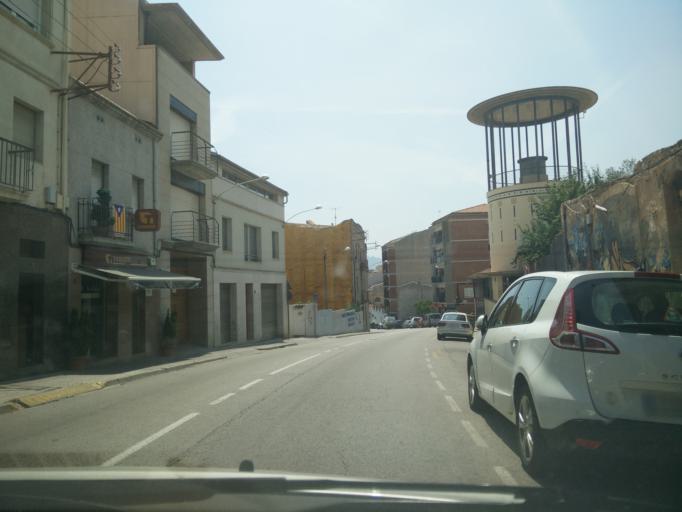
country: ES
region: Catalonia
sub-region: Provincia de Barcelona
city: Manresa
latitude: 41.7332
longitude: 1.8320
